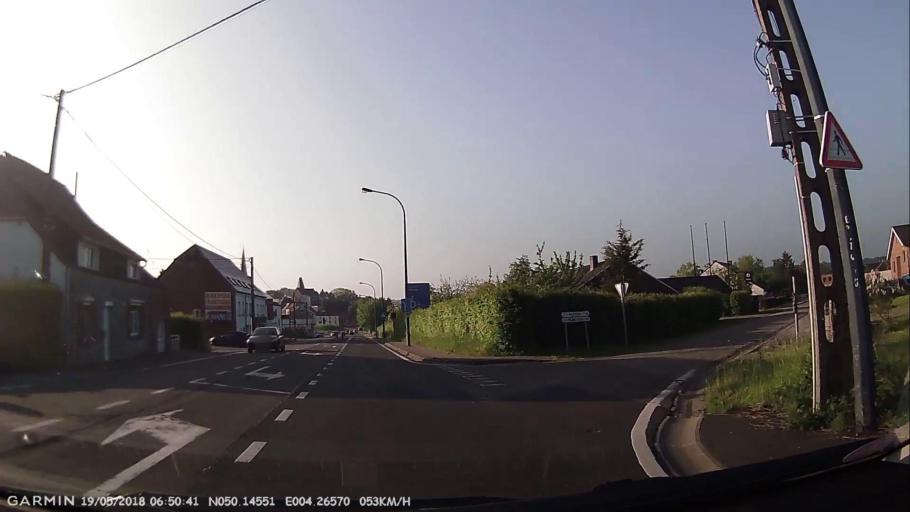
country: BE
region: Wallonia
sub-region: Province du Hainaut
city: Froidchapelle
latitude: 50.1453
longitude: 4.2659
